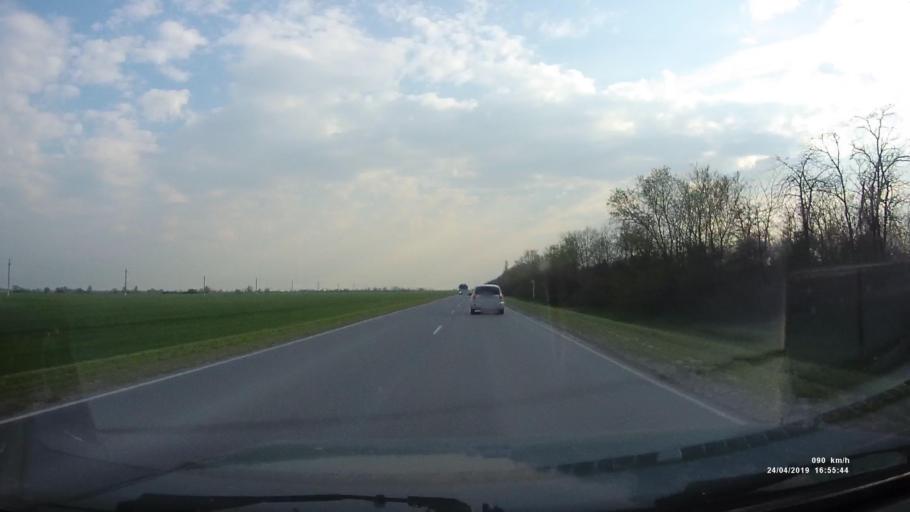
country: RU
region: Rostov
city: Proletarsk
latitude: 46.6604
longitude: 41.6850
